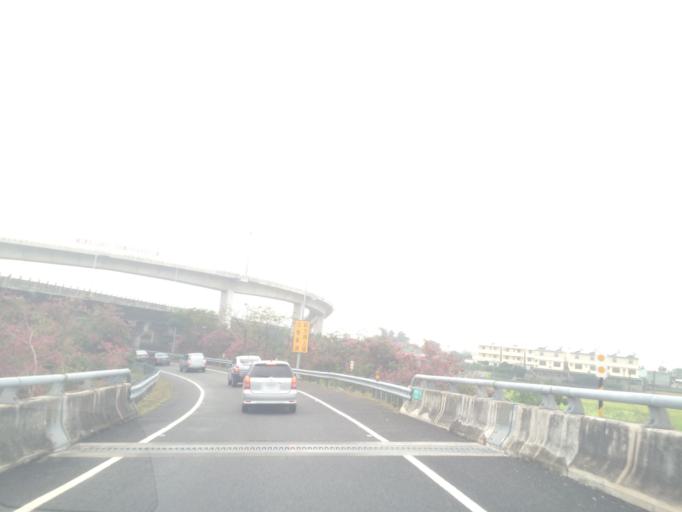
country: TW
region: Taiwan
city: Zhongxing New Village
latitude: 24.0287
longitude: 120.6691
